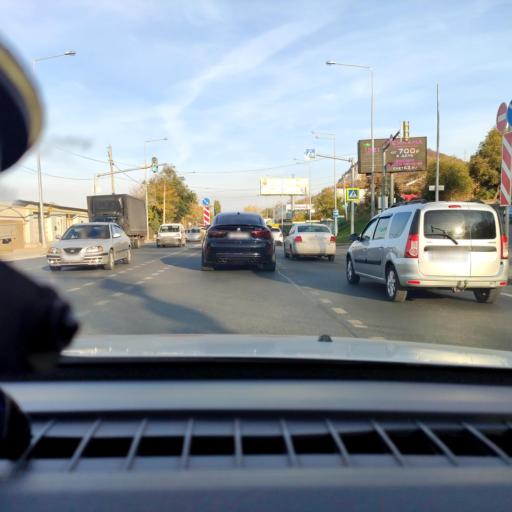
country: RU
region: Samara
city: Volzhskiy
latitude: 53.3824
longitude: 50.1663
